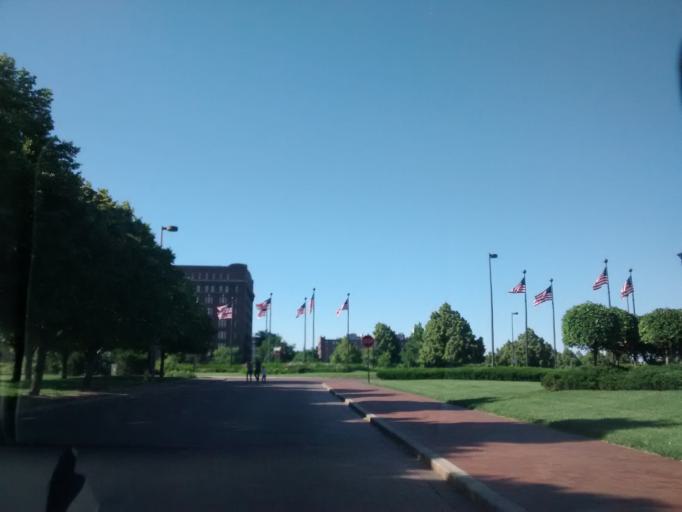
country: US
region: Nebraska
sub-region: Douglas County
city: Omaha
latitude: 41.2558
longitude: -95.9279
